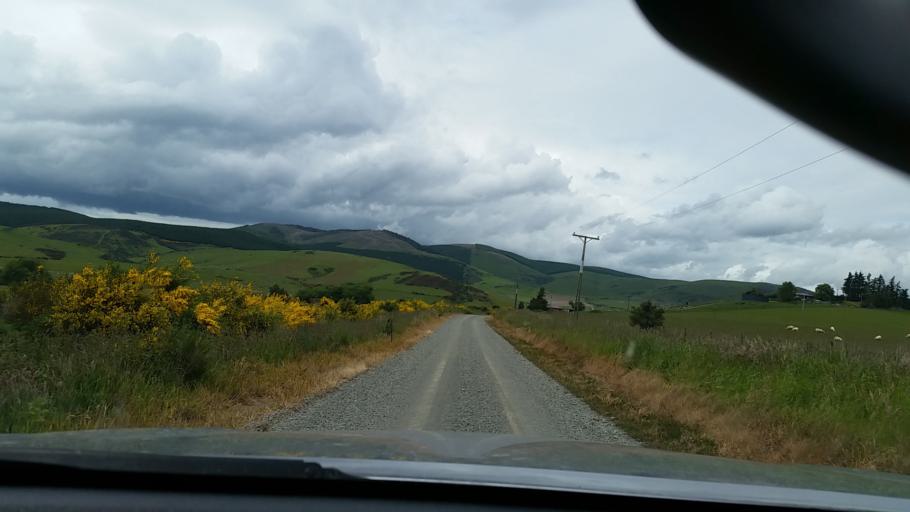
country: NZ
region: Southland
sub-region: Southland District
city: Winton
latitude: -45.8507
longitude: 168.1521
